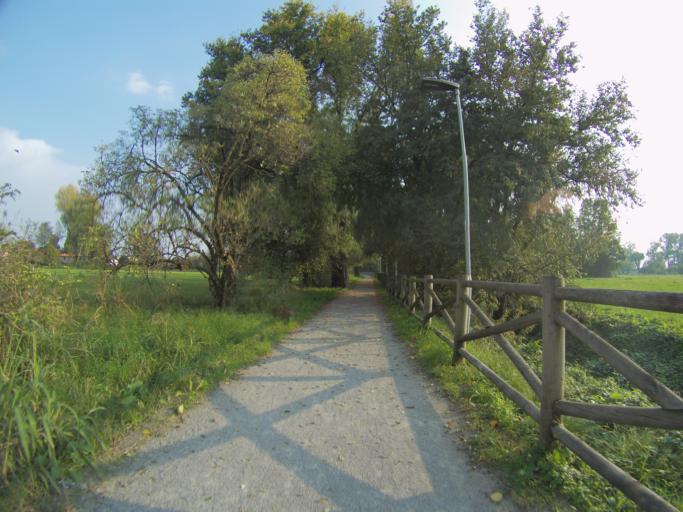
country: IT
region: Lombardy
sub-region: Citta metropolitana di Milano
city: Vignate
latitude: 45.4874
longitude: 9.3772
